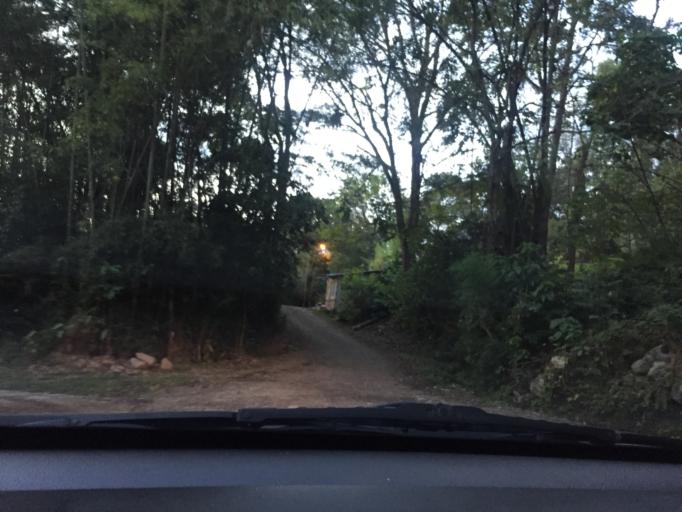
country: CO
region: Cundinamarca
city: Zipacon
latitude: 4.7122
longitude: -74.4107
